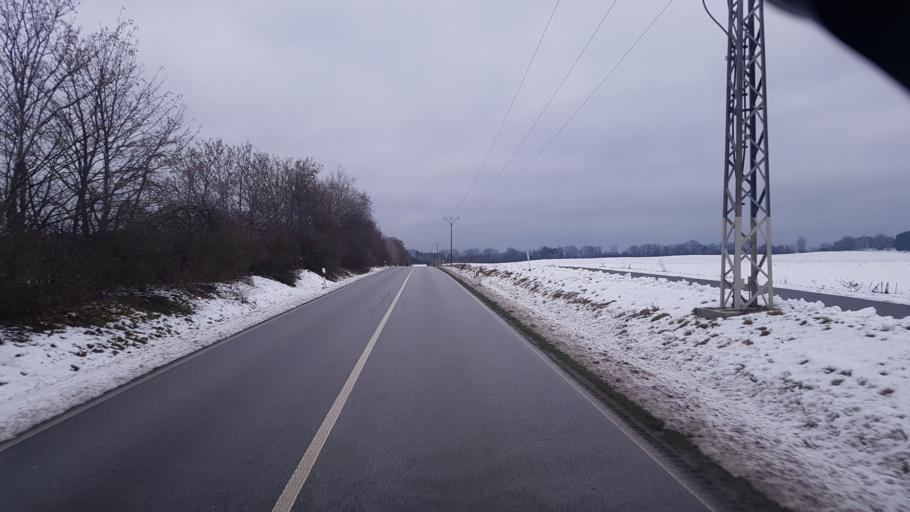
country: DE
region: Brandenburg
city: Lawitz
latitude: 52.1353
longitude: 14.5996
